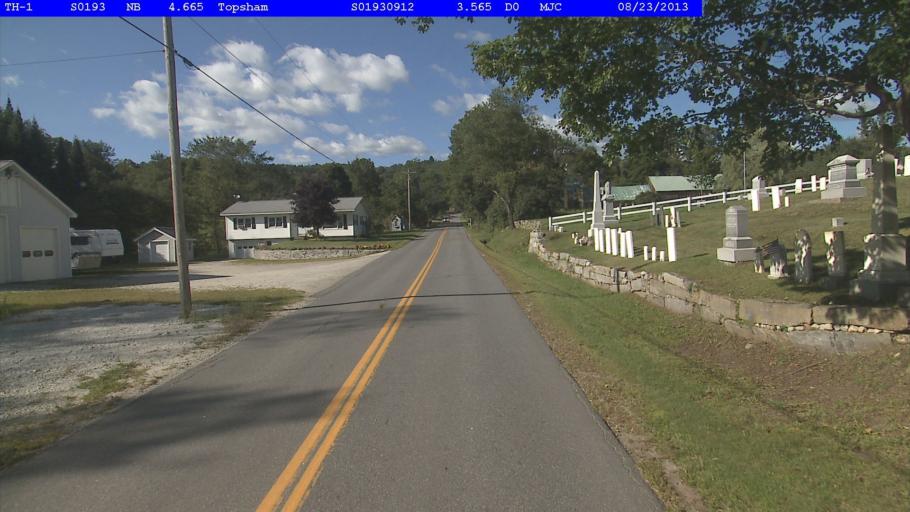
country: US
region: New Hampshire
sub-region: Grafton County
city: Haverhill
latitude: 44.1187
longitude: -72.2329
